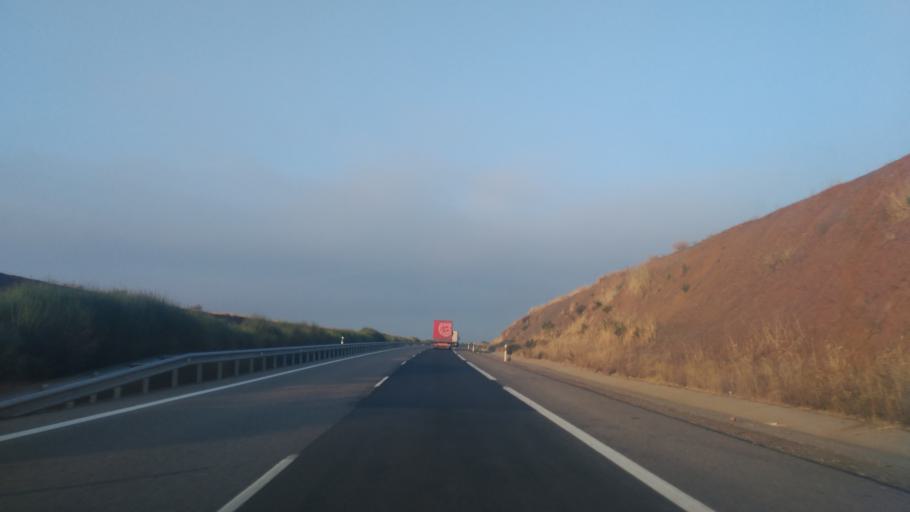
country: ES
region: Castille and Leon
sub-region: Provincia de Salamanca
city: Doninos de Salamanca
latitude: 40.9521
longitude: -5.7379
